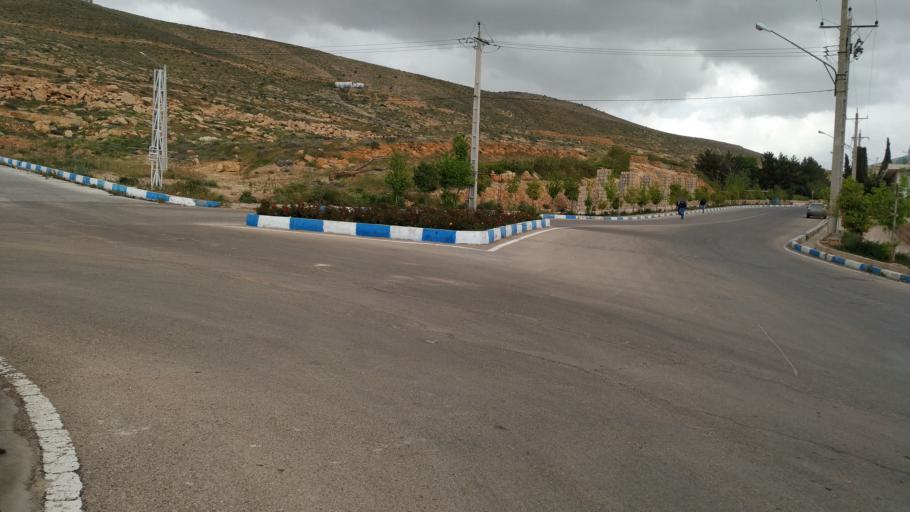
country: IR
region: Fars
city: Shiraz
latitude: 29.7673
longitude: 52.4804
